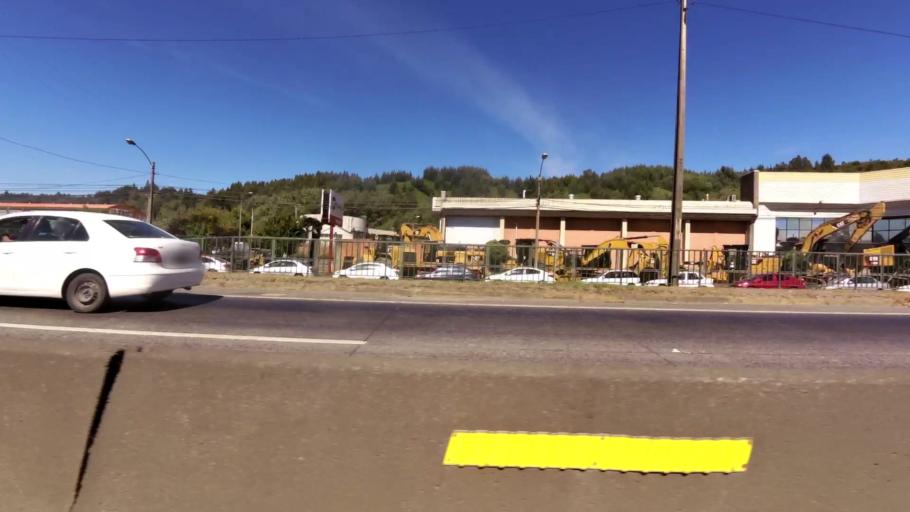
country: CL
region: Biobio
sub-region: Provincia de Concepcion
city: Concepcion
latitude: -36.8072
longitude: -73.0242
